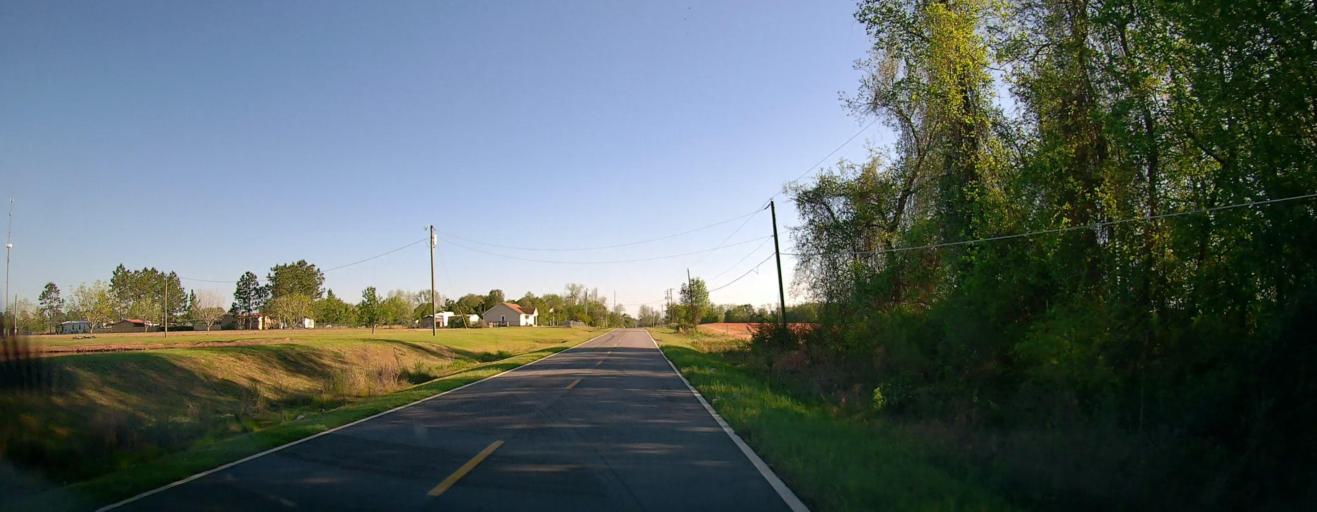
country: US
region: Georgia
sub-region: Ben Hill County
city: Fitzgerald
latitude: 31.7393
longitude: -83.2802
